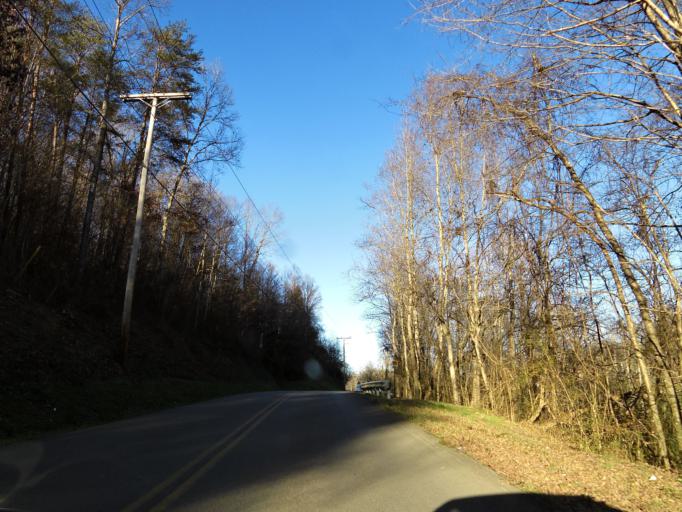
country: US
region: Tennessee
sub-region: Anderson County
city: Oak Ridge
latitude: 36.0912
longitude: -84.2331
